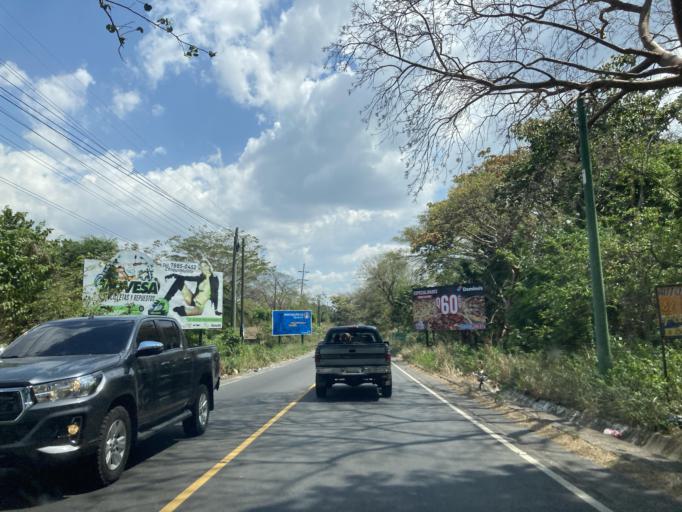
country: GT
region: Santa Rosa
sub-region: Municipio de Chiquimulilla
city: Chiquimulilla
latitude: 14.0683
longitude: -90.3873
